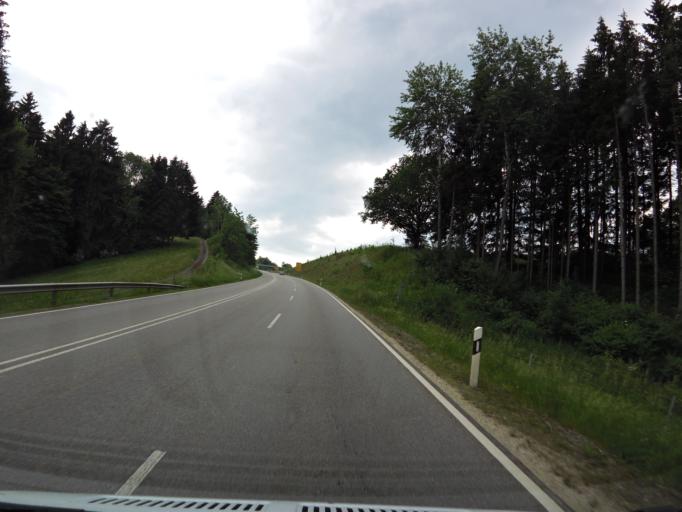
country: DE
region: Bavaria
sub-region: Lower Bavaria
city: Witzmannsberg
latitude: 48.6895
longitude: 13.4318
